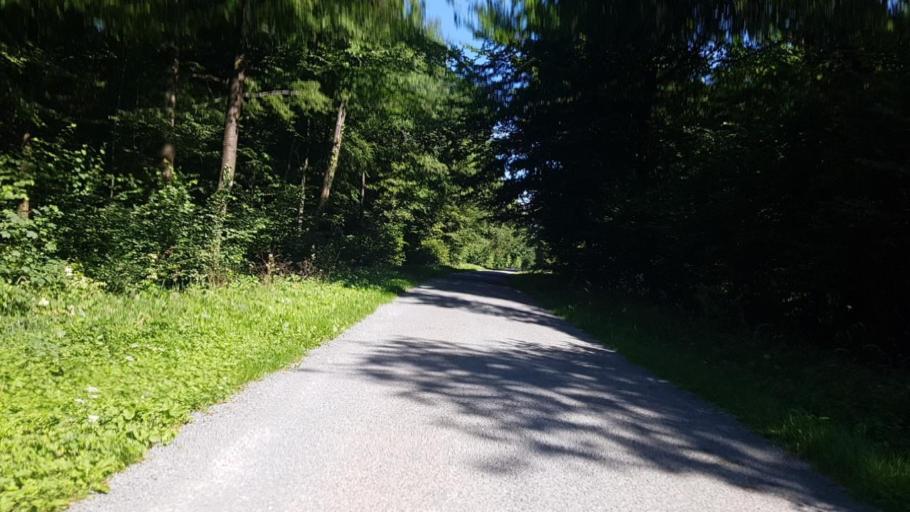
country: BE
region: Wallonia
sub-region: Province du Hainaut
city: Momignies
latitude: 50.0330
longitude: 4.2003
